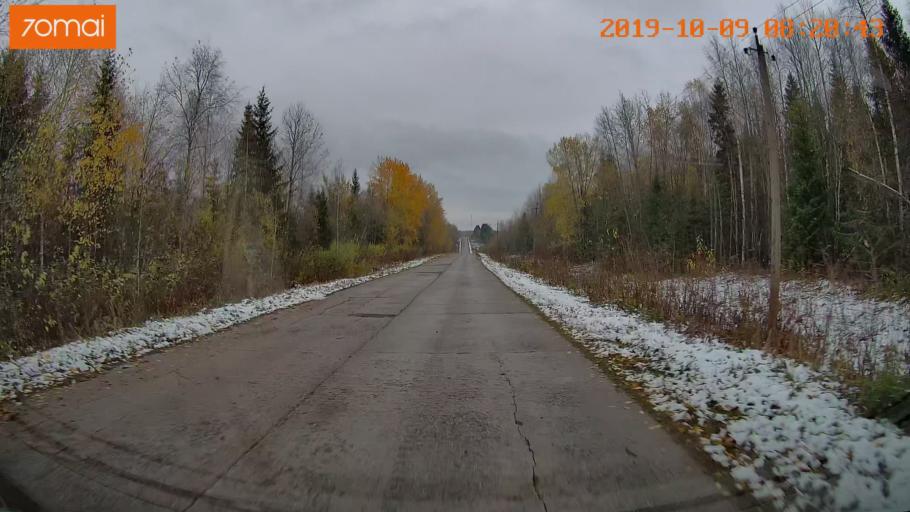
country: RU
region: Vologda
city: Gryazovets
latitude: 58.7426
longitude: 40.2643
